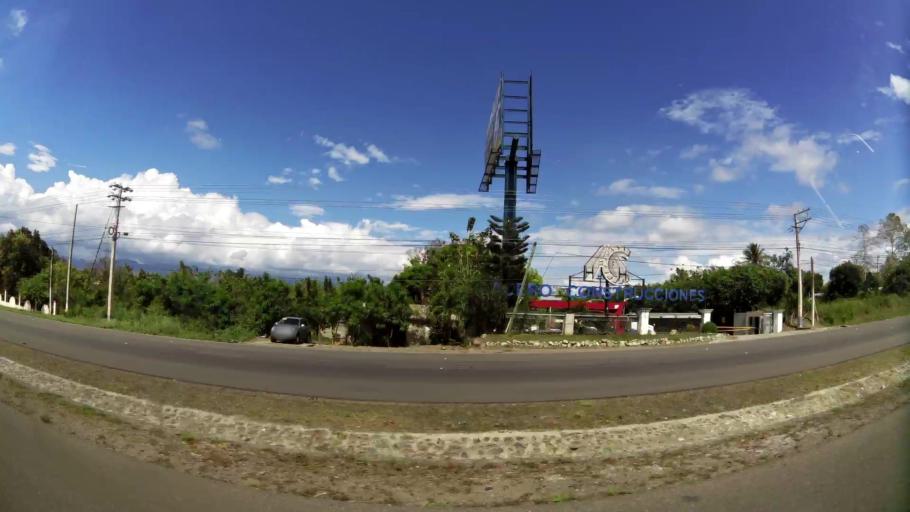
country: DO
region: Santiago
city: Licey al Medio
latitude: 19.3766
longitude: -70.6070
